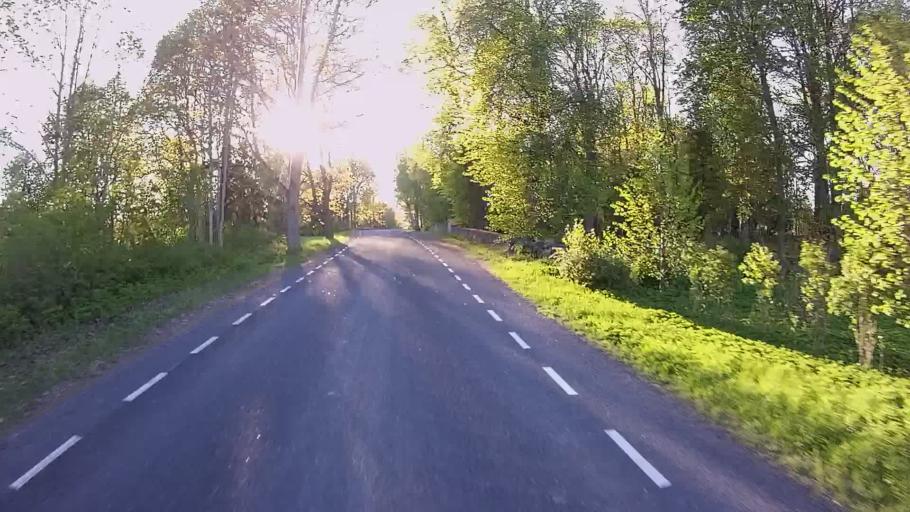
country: EE
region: Jogevamaa
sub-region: Poltsamaa linn
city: Poltsamaa
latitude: 58.5250
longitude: 25.9598
